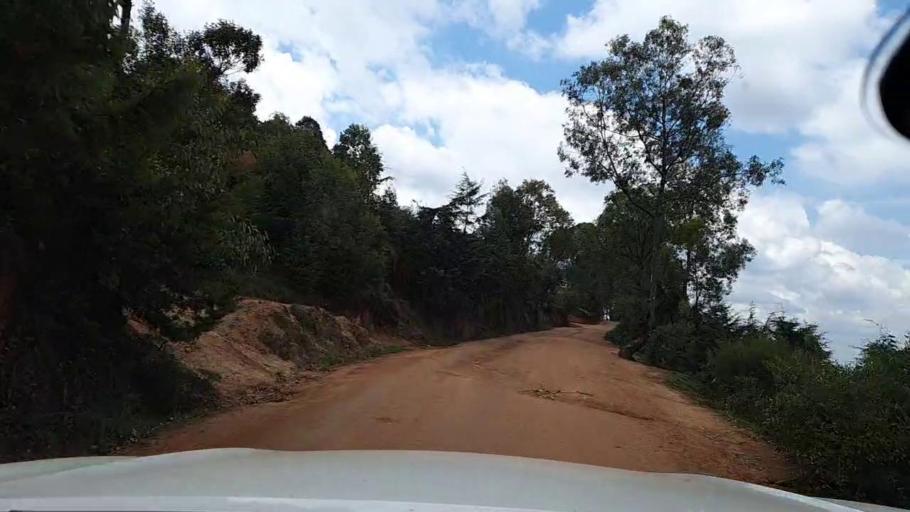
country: RW
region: Southern Province
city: Nzega
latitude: -2.7098
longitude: 29.5235
